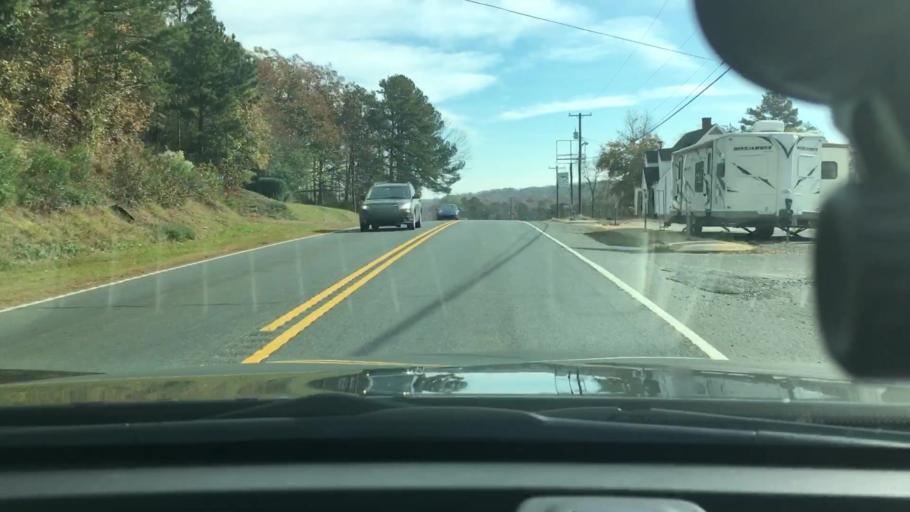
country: US
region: North Carolina
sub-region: Stanly County
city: Badin
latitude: 35.3151
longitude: -80.1036
